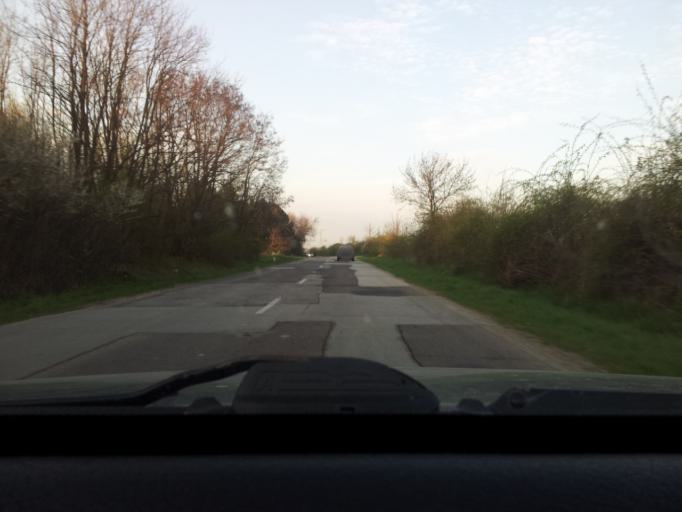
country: SK
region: Nitriansky
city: Tlmace
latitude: 48.2599
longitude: 18.4418
